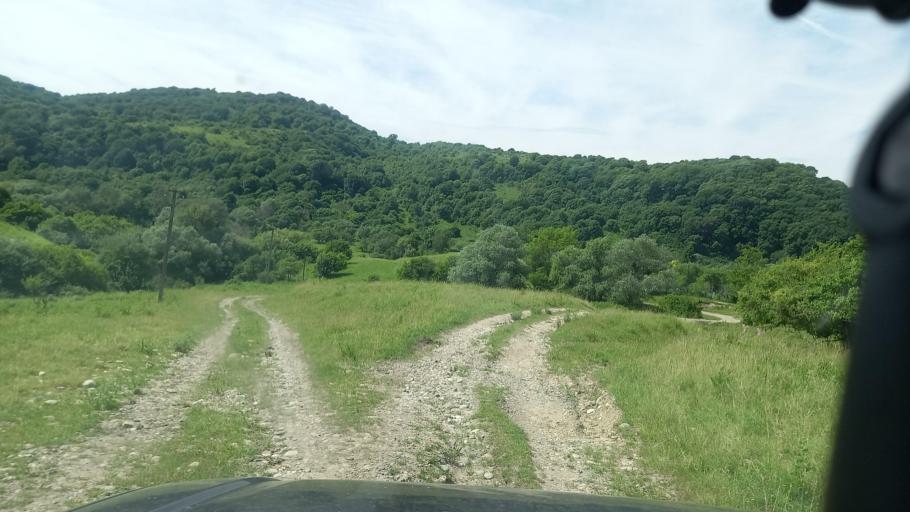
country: RU
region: Karachayevo-Cherkesiya
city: Kurdzhinovo
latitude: 44.1443
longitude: 41.0577
